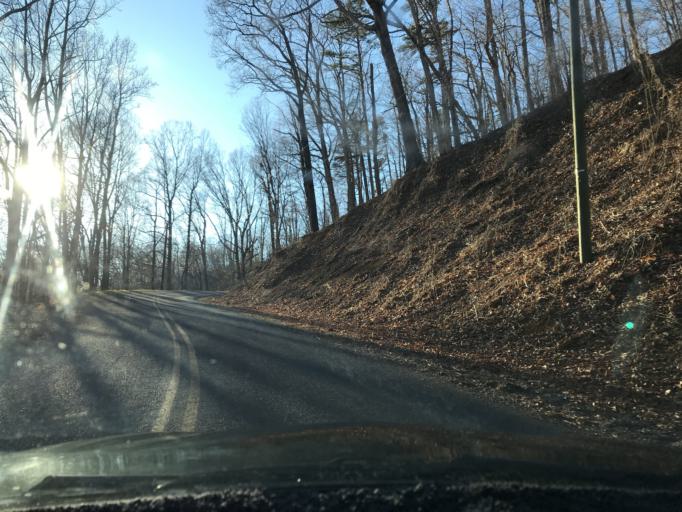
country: US
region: Virginia
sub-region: Botetourt County
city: Buchanan
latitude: 37.4764
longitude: -79.6571
